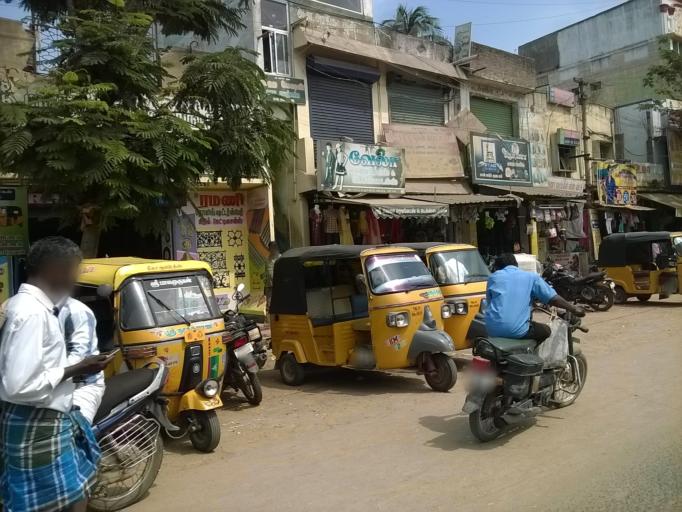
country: IN
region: Tamil Nadu
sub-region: Cuddalore
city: Panruti
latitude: 11.7724
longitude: 79.5525
